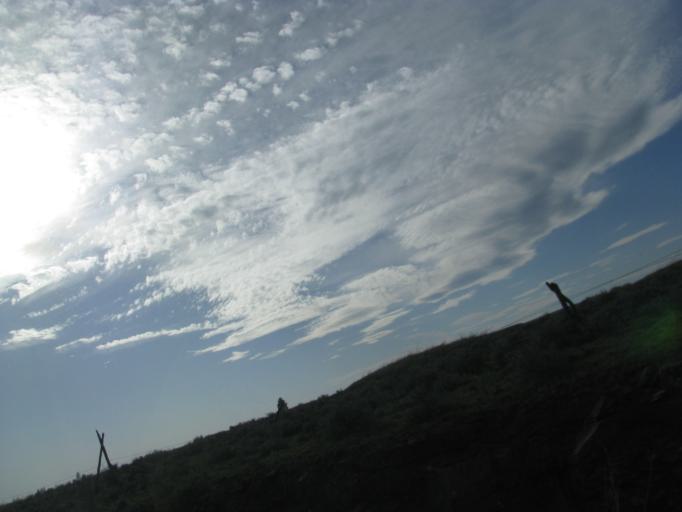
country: US
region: Washington
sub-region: Spokane County
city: Medical Lake
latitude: 47.3502
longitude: -117.8591
